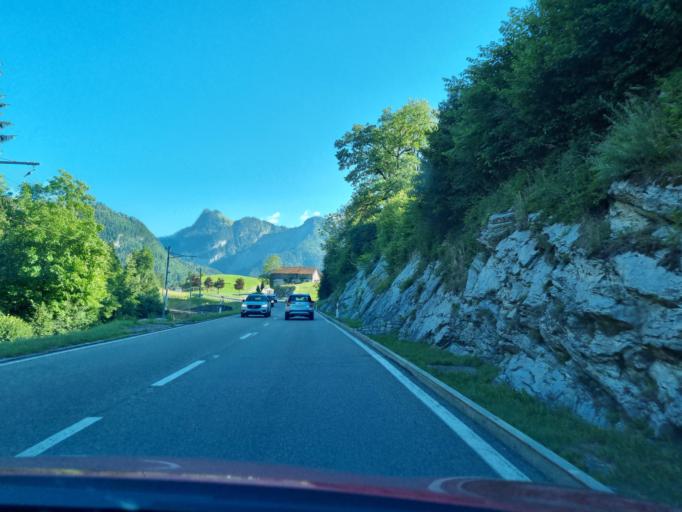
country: CH
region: Fribourg
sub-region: Gruyere District
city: Gruyeres
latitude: 46.5047
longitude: 7.0510
